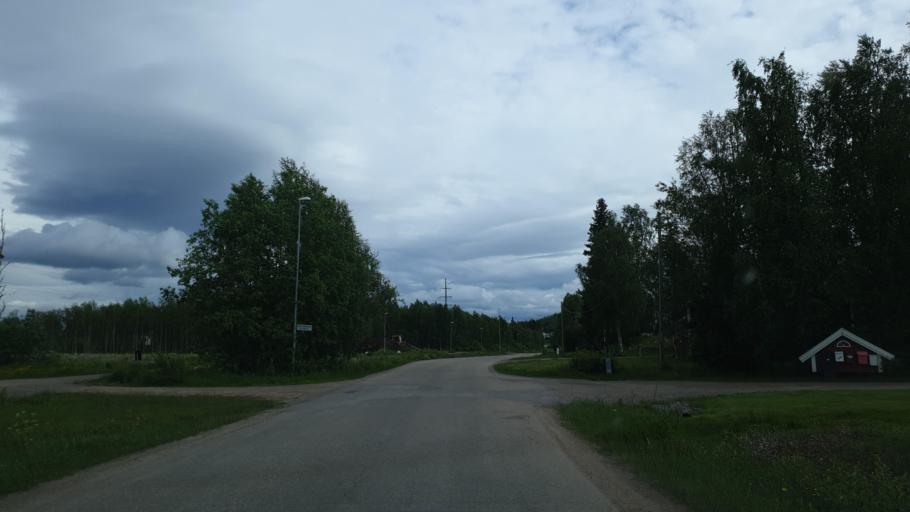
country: SE
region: Norrbotten
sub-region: Gallivare Kommun
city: Gaellivare
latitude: 67.1311
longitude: 20.6439
